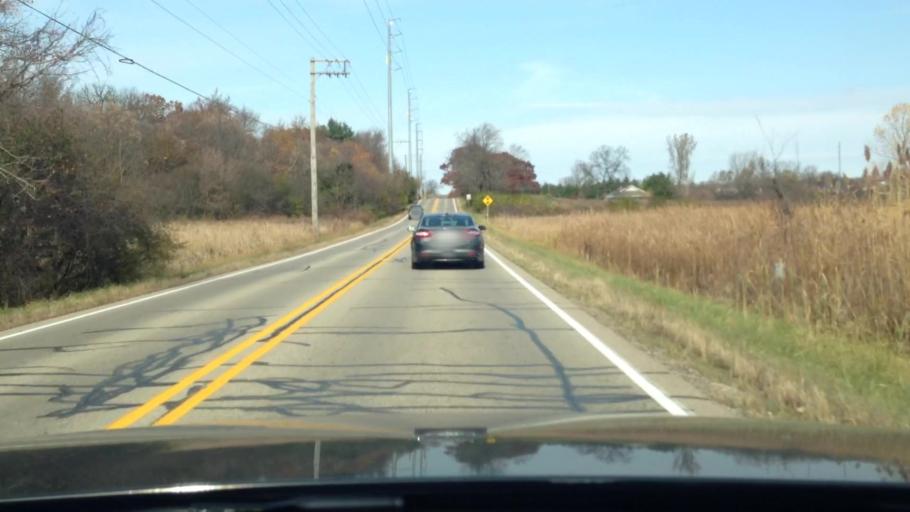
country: US
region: Illinois
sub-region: McHenry County
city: Woodstock
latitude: 42.2934
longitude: -88.4527
